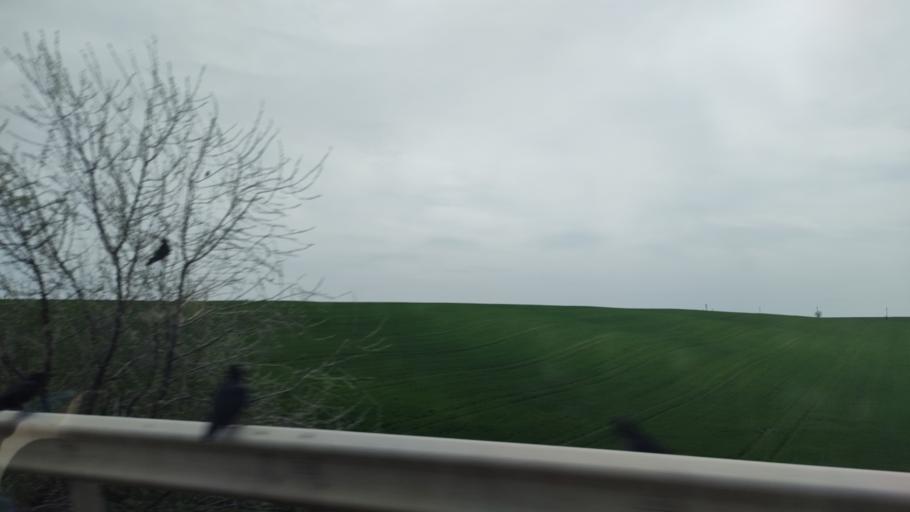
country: RO
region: Constanta
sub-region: Comuna Deleni
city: Pietreni
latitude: 44.0916
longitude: 28.0645
